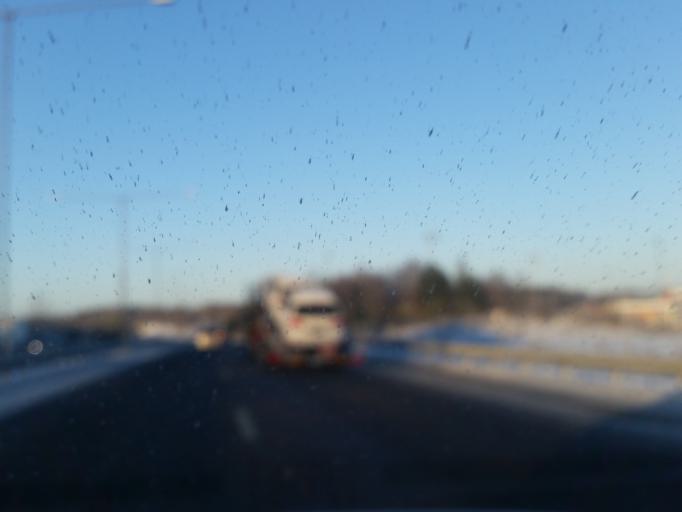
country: SE
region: Stockholm
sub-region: Sodertalje Kommun
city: Soedertaelje
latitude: 59.1851
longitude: 17.5750
